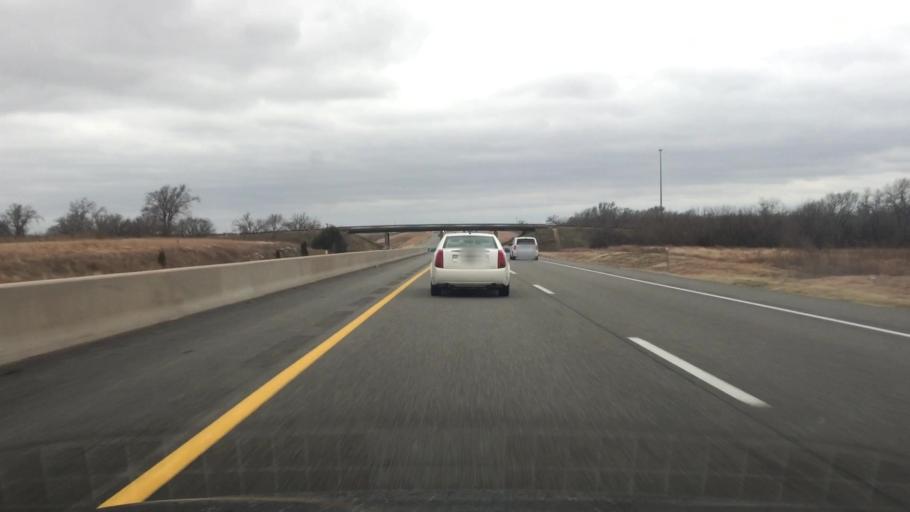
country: US
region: Kansas
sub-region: Butler County
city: Towanda
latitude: 37.7821
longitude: -96.9506
